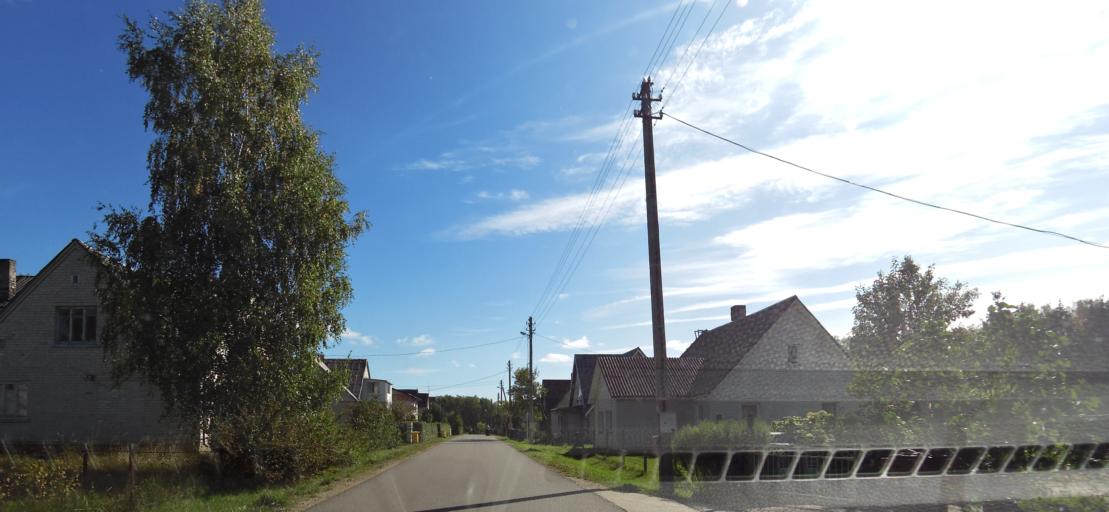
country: LT
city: Skaidiskes
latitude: 54.6062
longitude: 25.3779
